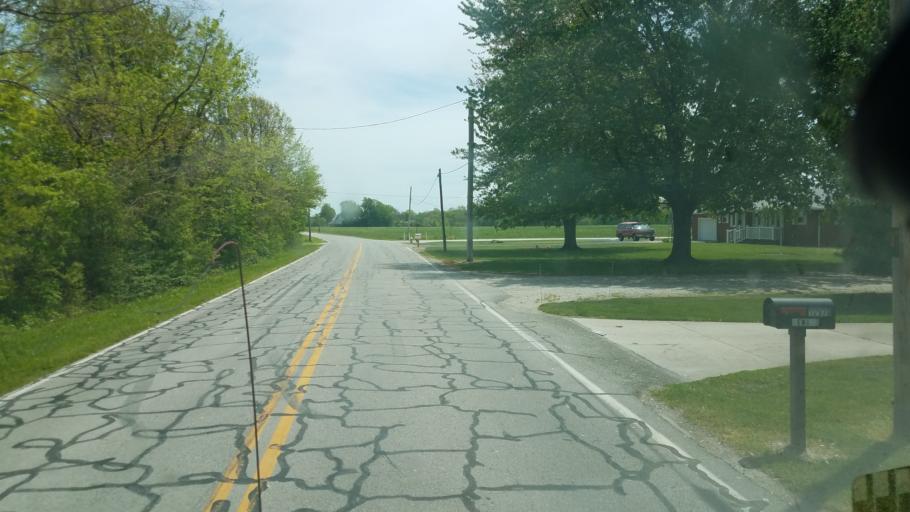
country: US
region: Ohio
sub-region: Ottawa County
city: Oak Harbor
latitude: 41.4972
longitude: -83.1751
